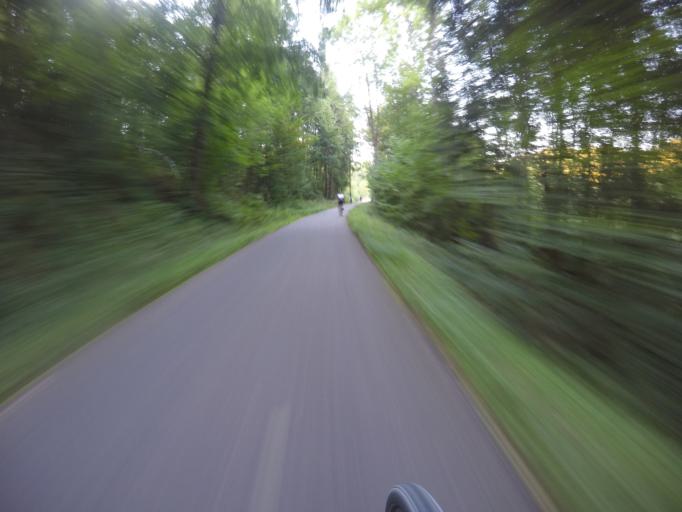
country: DE
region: Baden-Wuerttemberg
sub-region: Regierungsbezirk Stuttgart
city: Steinenbronn
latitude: 48.6801
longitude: 9.1253
